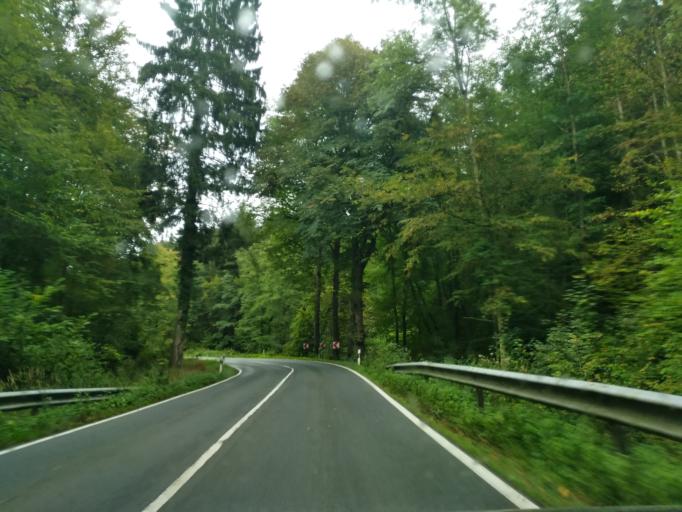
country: DE
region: North Rhine-Westphalia
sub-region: Regierungsbezirk Koln
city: Bad Honnef
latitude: 50.6566
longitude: 7.2717
